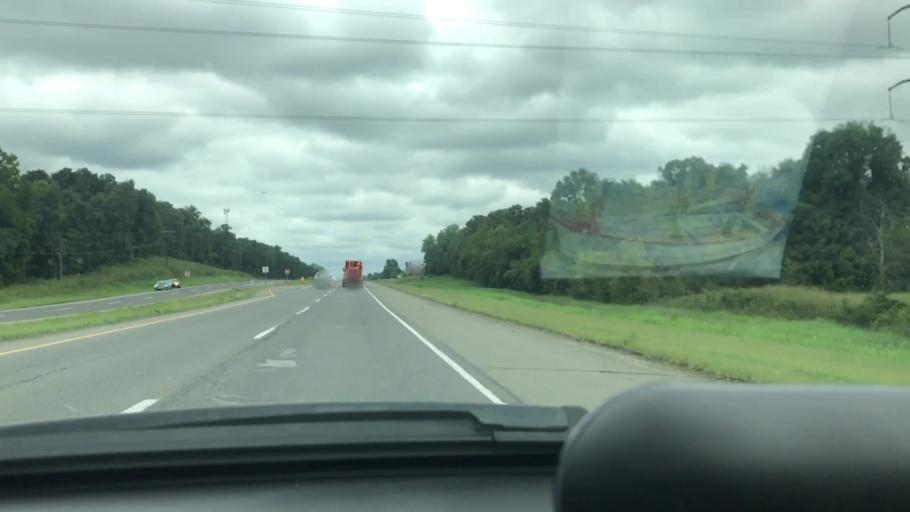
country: US
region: Oklahoma
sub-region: Muskogee County
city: Muskogee
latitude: 35.8205
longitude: -95.4026
